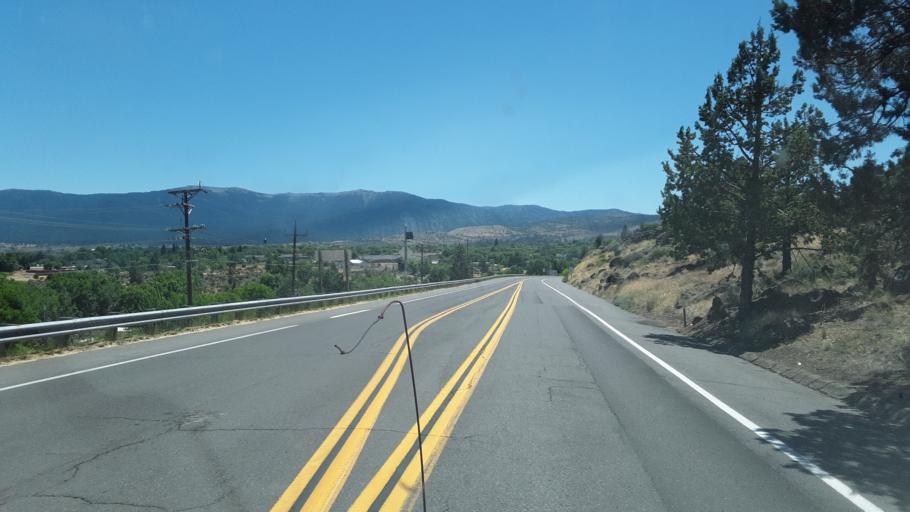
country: US
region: California
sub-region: Lassen County
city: Susanville
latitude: 40.4281
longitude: -120.6397
